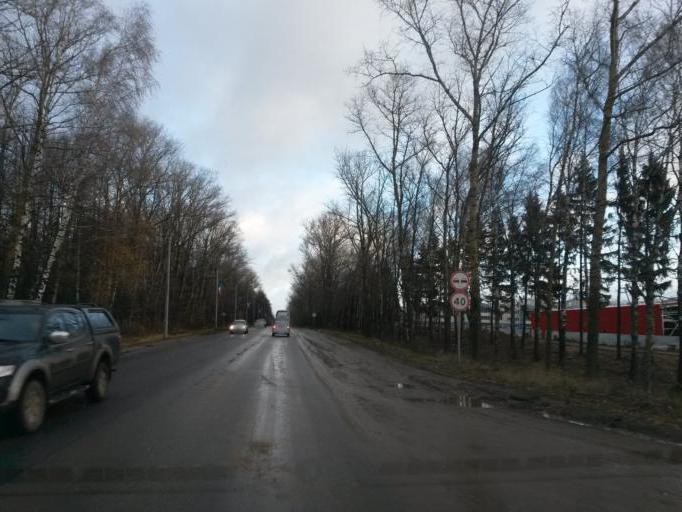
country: RU
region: Jaroslavl
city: Pereslavl'-Zalesskiy
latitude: 56.7526
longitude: 38.8631
